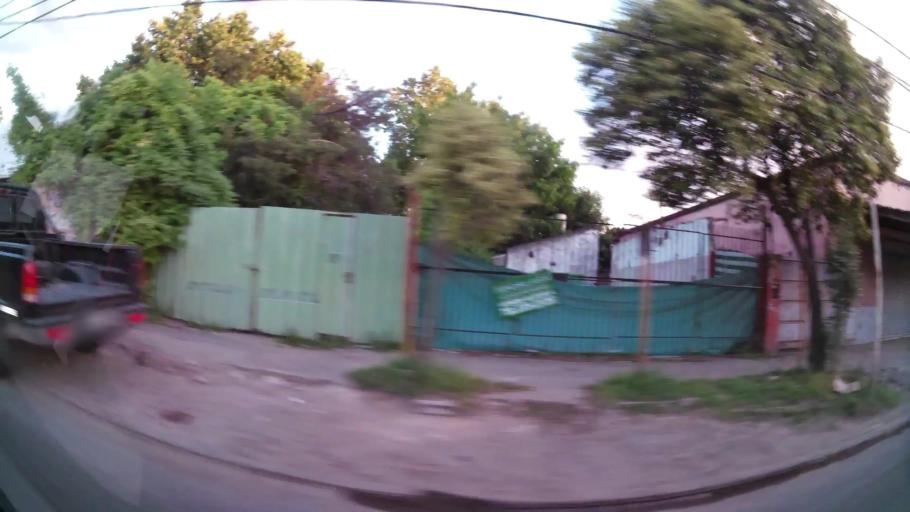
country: AR
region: Buenos Aires
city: Santa Catalina - Dique Lujan
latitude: -34.4817
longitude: -58.7760
